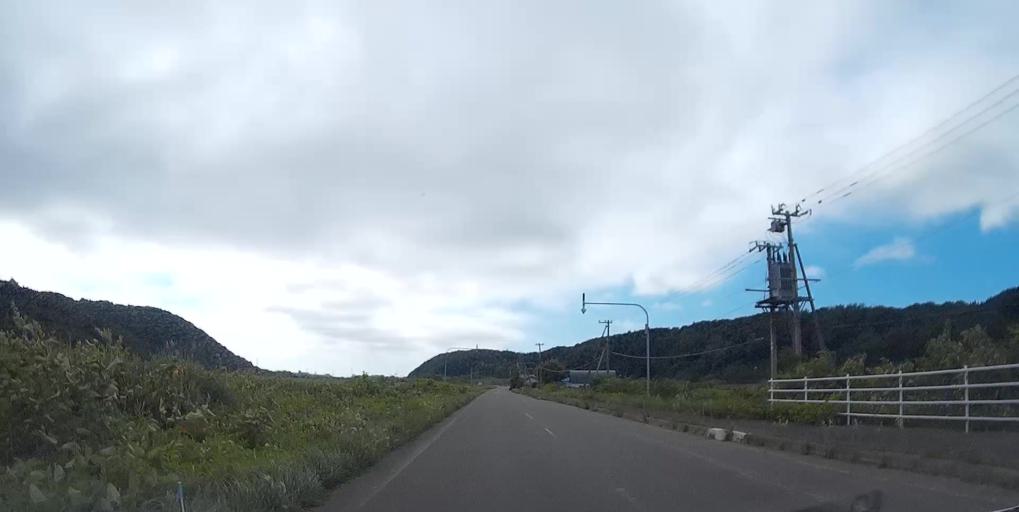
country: JP
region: Hokkaido
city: Kamiiso
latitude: 41.9731
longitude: 140.1635
